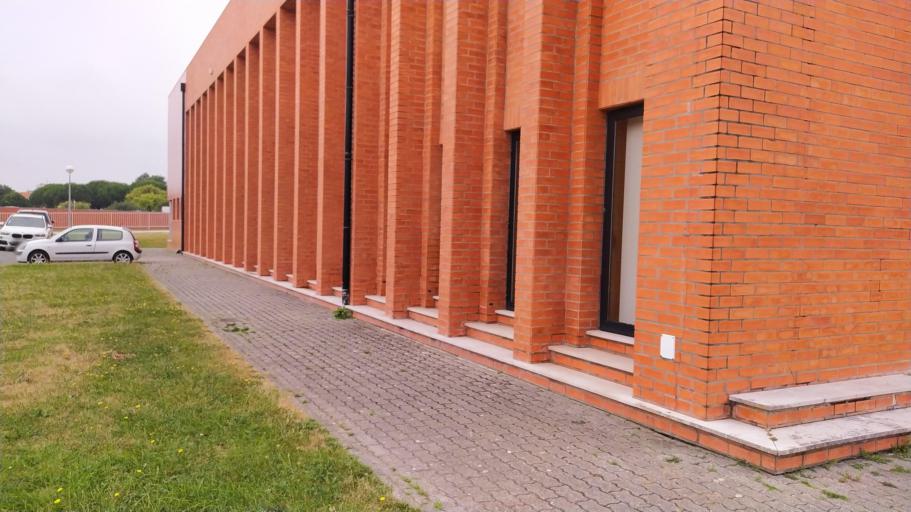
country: PT
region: Aveiro
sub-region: Aveiro
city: Aveiro
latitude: 40.6342
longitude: -8.6603
